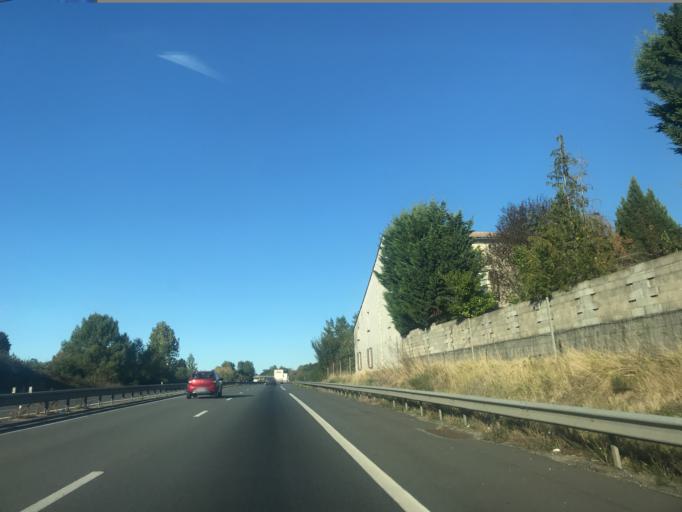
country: FR
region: Poitou-Charentes
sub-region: Departement de la Charente-Maritime
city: Montlieu-la-Garde
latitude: 45.2288
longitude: -0.2813
